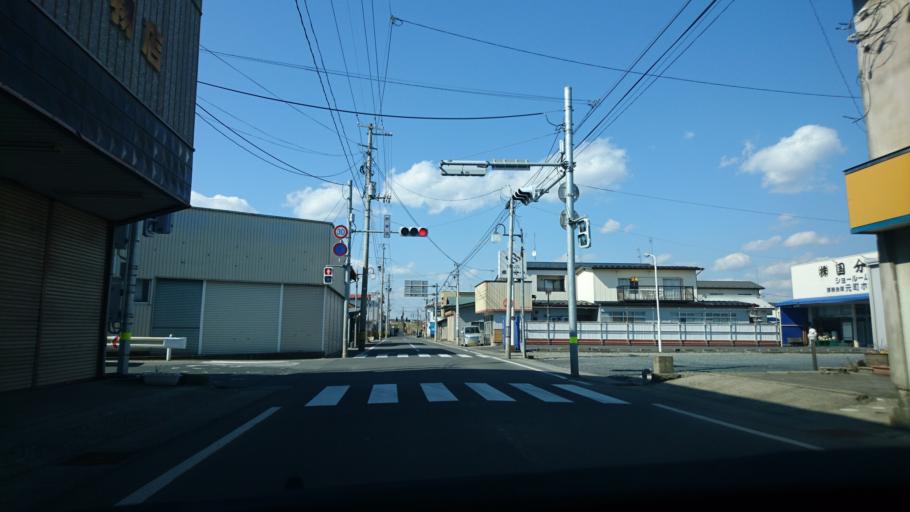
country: JP
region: Miyagi
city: Wakuya
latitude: 38.7075
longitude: 141.2882
